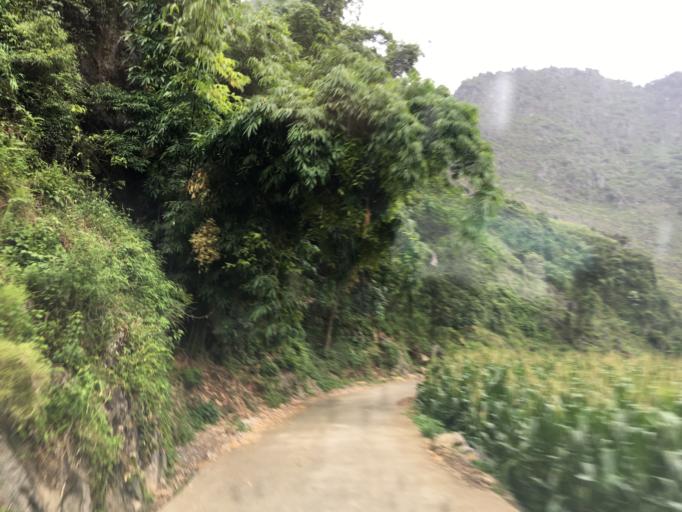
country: CN
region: Guangxi Zhuangzu Zizhiqu
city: Xinzhou
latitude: 24.9918
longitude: 105.6404
